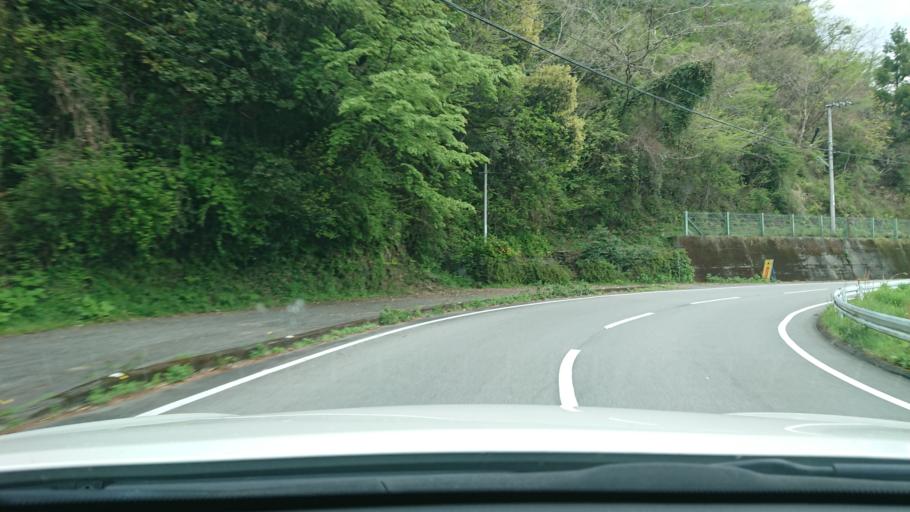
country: JP
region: Tokushima
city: Ishii
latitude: 33.9076
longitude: 134.4199
